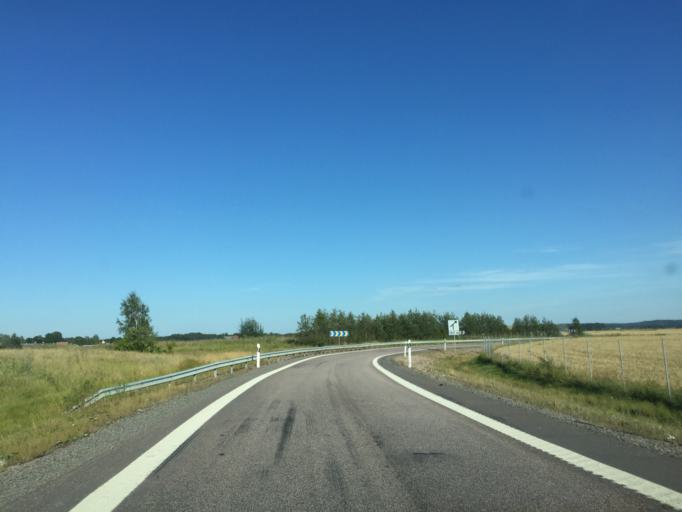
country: SE
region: Vaestmanland
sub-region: Arboga Kommun
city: Arboga
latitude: 59.4283
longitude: 15.8883
